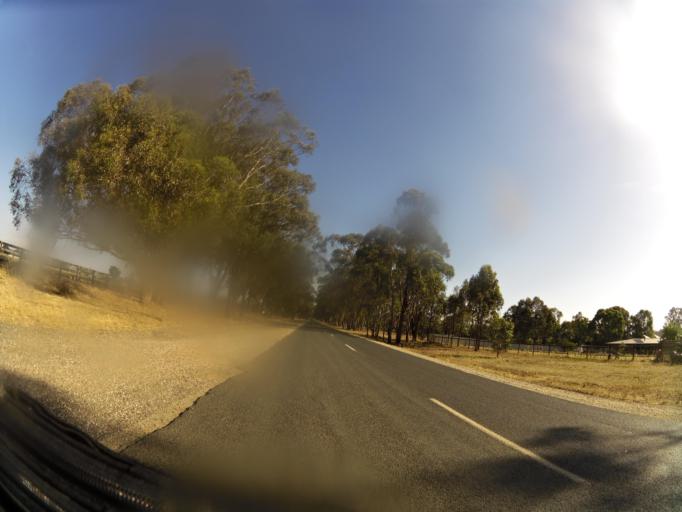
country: AU
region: Victoria
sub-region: Murrindindi
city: Kinglake West
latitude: -36.9632
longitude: 145.1082
